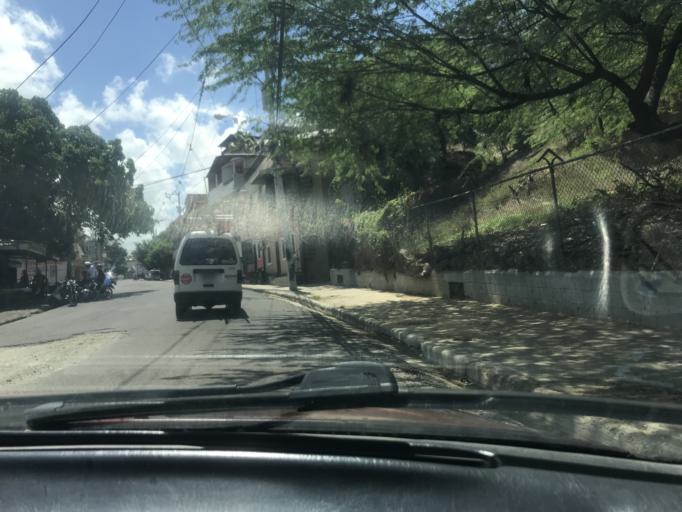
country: DO
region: Santiago
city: Santiago de los Caballeros
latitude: 19.4662
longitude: -70.7047
